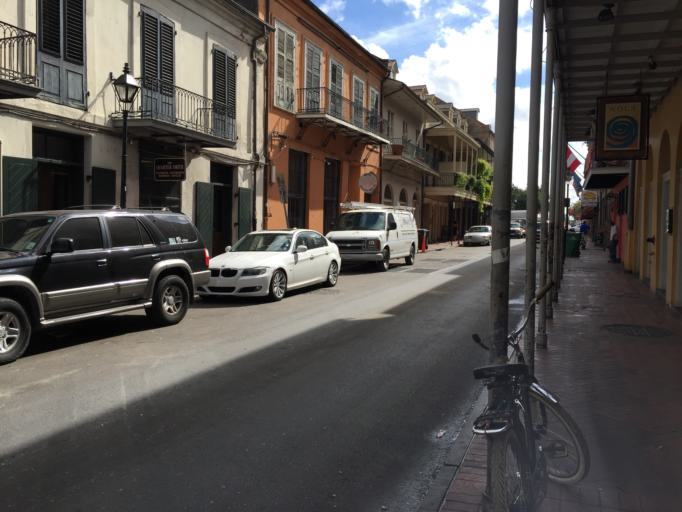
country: US
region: Louisiana
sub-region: Orleans Parish
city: New Orleans
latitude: 29.9557
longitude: -90.0651
